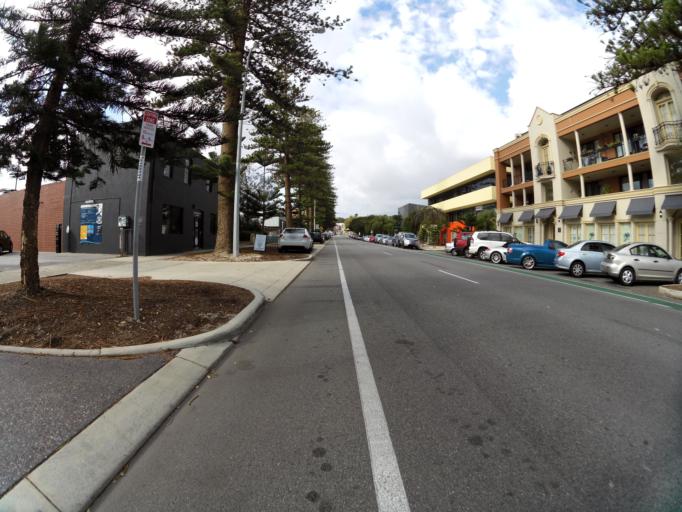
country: AU
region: Western Australia
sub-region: Fremantle
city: South Fremantle
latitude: -32.0581
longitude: 115.7476
